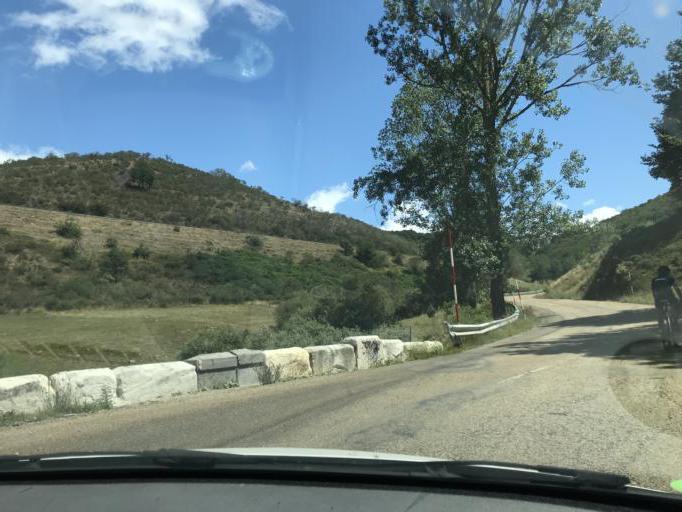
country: ES
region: Castille and Leon
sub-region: Provincia de Palencia
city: Polentinos
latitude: 43.0320
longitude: -4.4625
